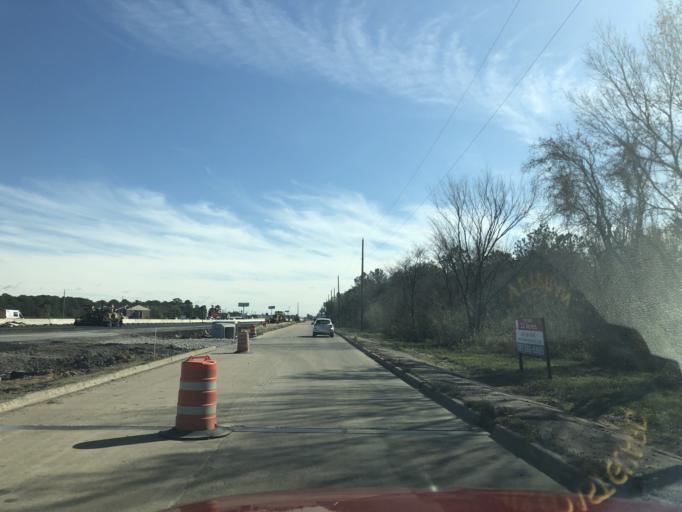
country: US
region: Texas
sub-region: Galveston County
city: Dickinson
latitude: 29.4624
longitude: -95.0883
